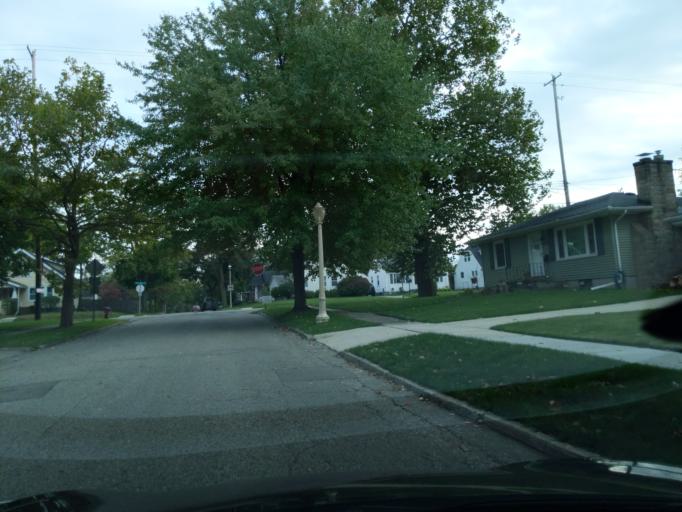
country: US
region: Michigan
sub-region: Ingham County
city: Lansing
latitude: 42.7123
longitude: -84.5328
